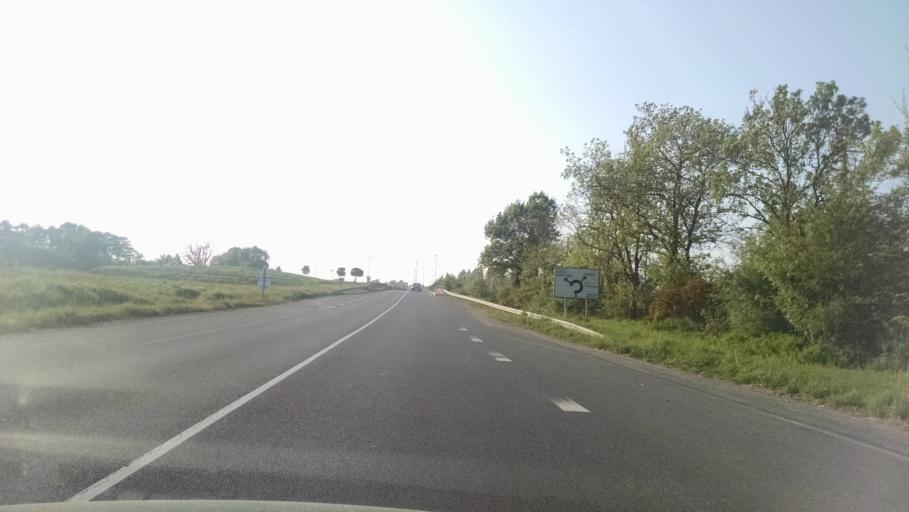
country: FR
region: Pays de la Loire
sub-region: Departement de la Loire-Atlantique
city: Gorges
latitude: 47.0930
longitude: -1.2967
